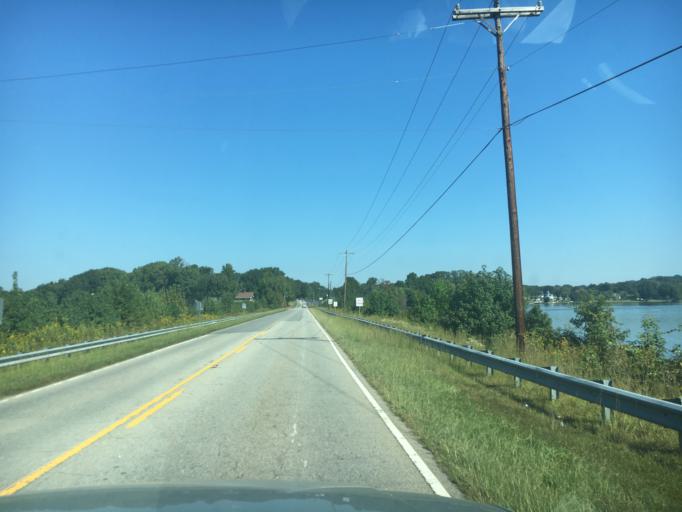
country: US
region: South Carolina
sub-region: Spartanburg County
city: Inman
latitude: 35.1111
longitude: -82.0404
